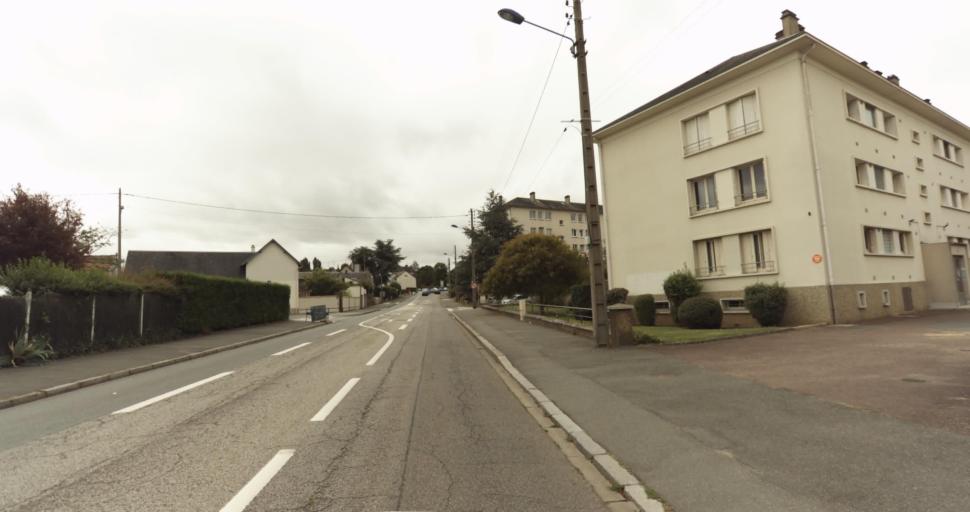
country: FR
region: Haute-Normandie
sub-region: Departement de l'Eure
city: Evreux
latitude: 49.0225
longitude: 1.1558
